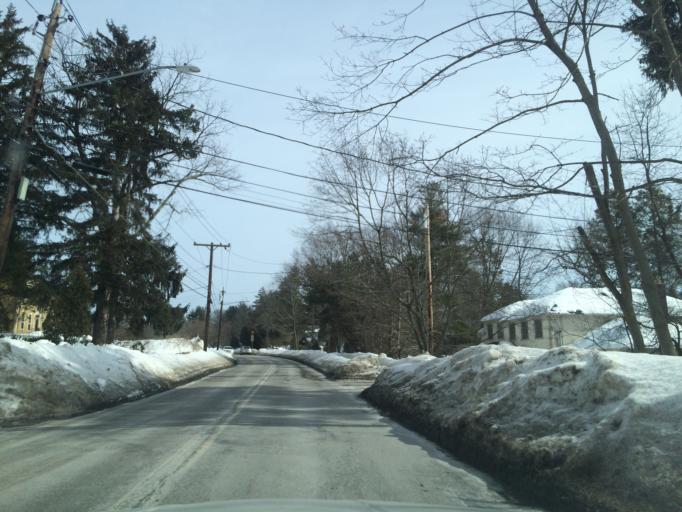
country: US
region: Massachusetts
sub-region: Middlesex County
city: Newton
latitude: 42.3010
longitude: -71.1814
